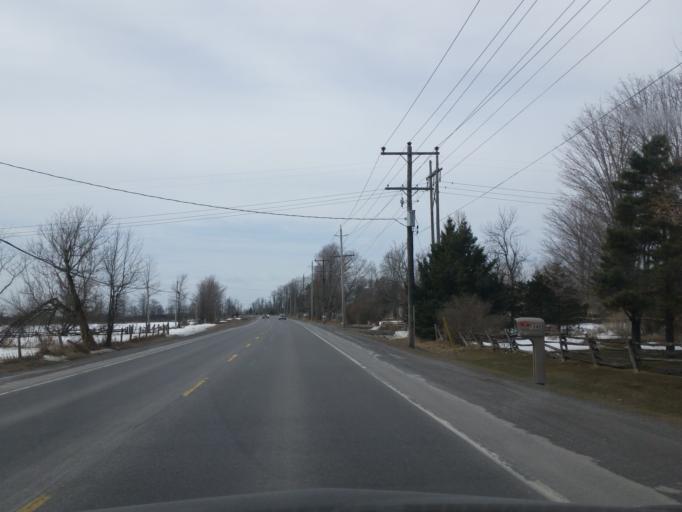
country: CA
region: Ontario
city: Skatepark
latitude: 44.2683
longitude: -76.7600
